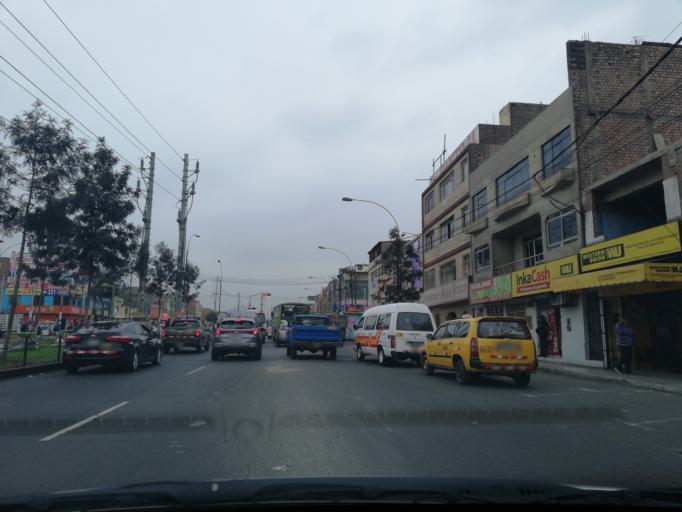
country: PE
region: Lima
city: Lima
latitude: -12.0321
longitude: -77.0655
